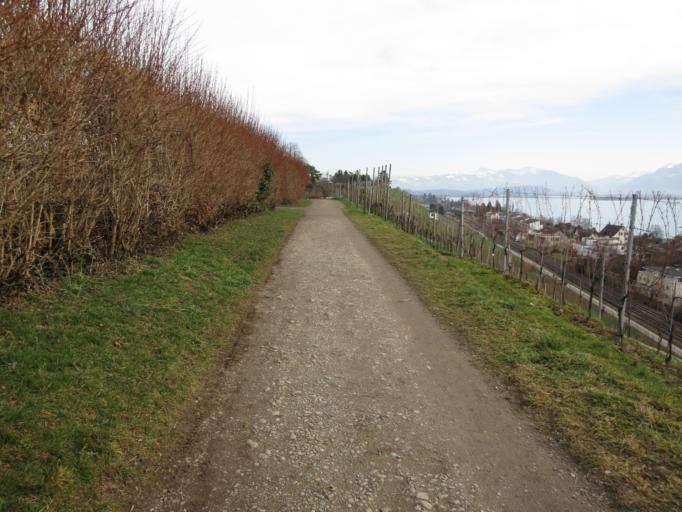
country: CH
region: Zurich
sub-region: Bezirk Meilen
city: Dorf
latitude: 47.2366
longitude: 8.7414
